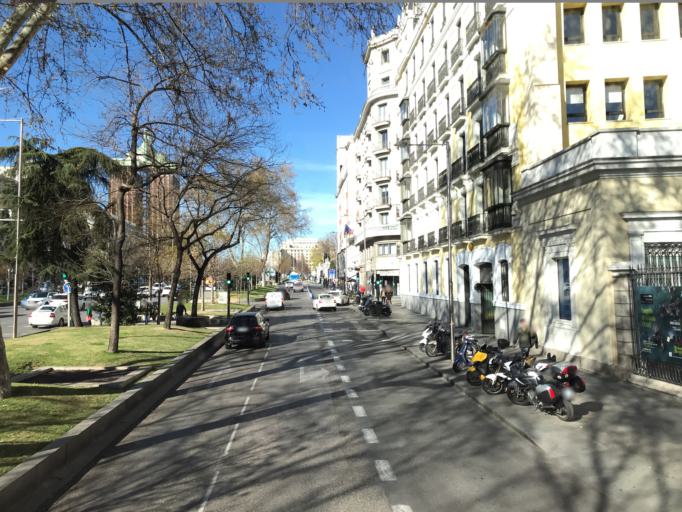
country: ES
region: Madrid
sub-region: Provincia de Madrid
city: City Center
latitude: 40.4217
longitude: -3.6915
